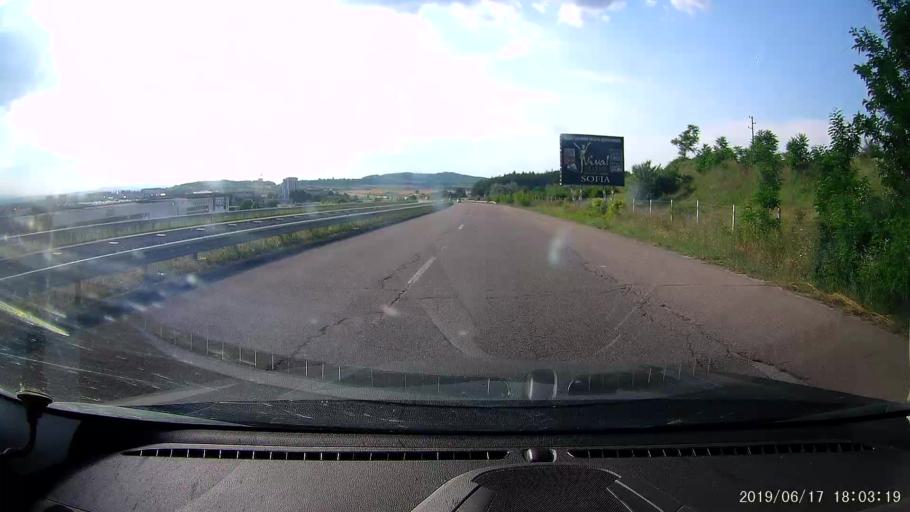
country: BG
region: Khaskovo
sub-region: Obshtina Svilengrad
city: Svilengrad
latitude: 41.7757
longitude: 26.2213
